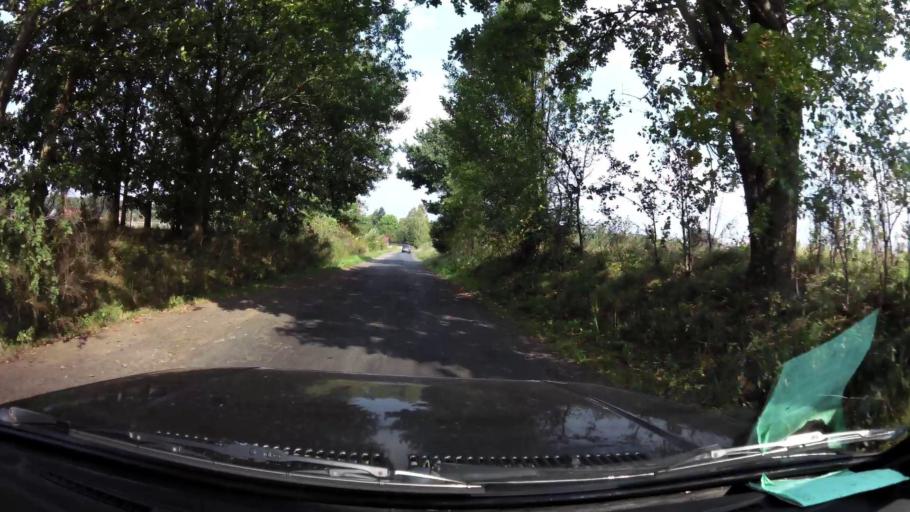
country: PL
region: West Pomeranian Voivodeship
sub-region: Powiat koszalinski
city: Bobolice
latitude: 54.1113
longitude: 16.5016
